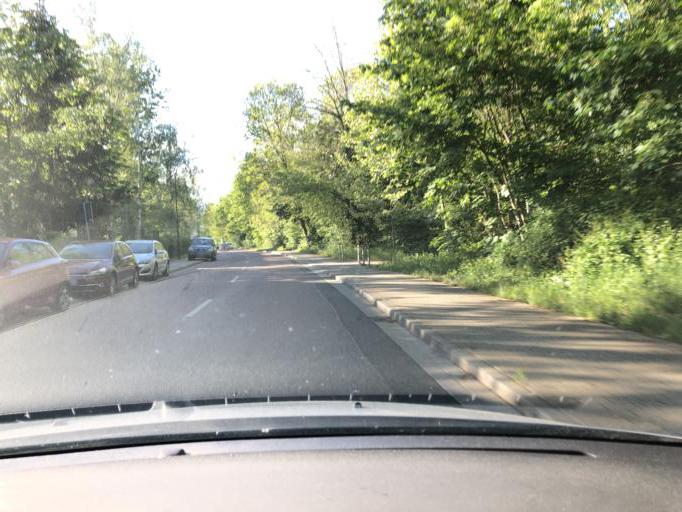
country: DE
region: Saxony
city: Markkleeberg
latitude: 51.2452
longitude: 12.3836
